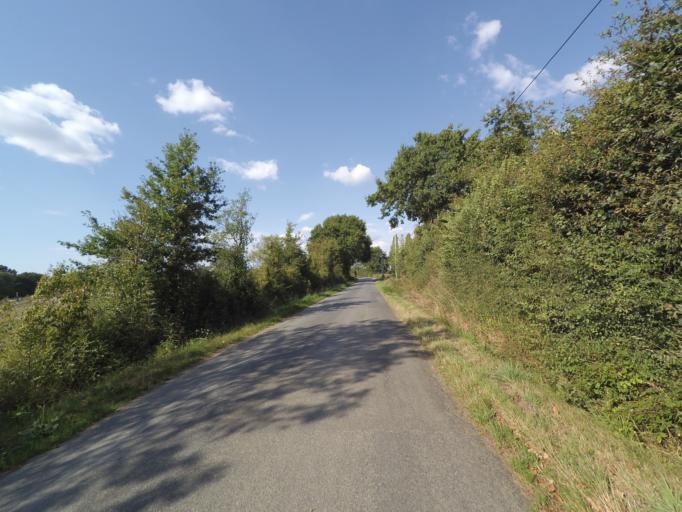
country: FR
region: Pays de la Loire
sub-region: Departement de la Loire-Atlantique
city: Vieillevigne
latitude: 46.9811
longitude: -1.4245
